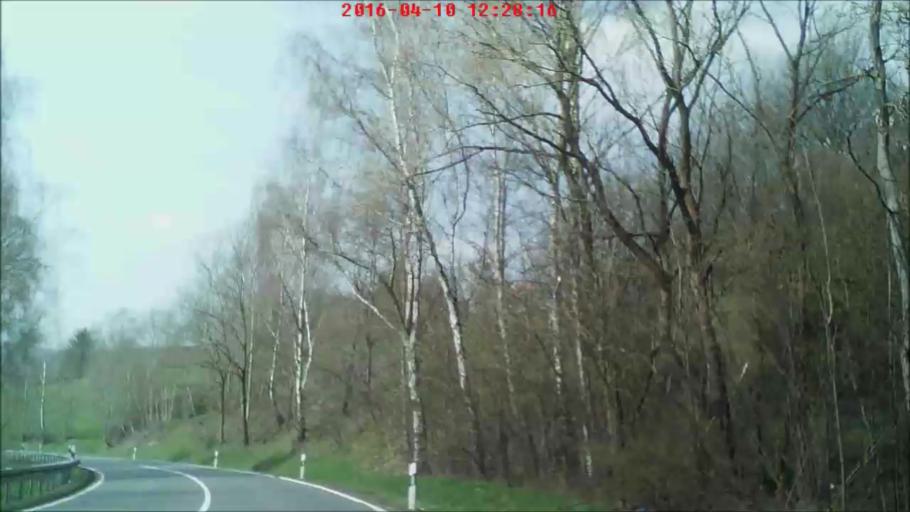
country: DE
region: Thuringia
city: Springstille
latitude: 50.6851
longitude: 10.5361
